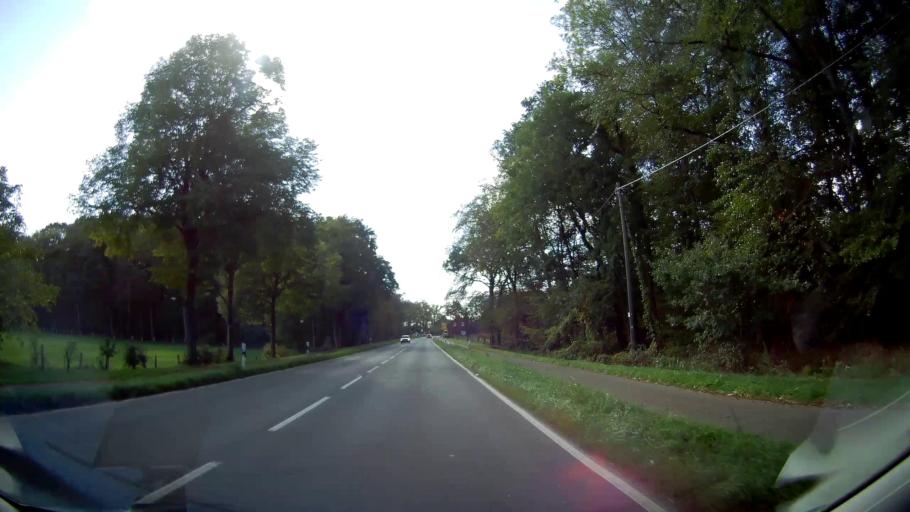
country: DE
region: North Rhine-Westphalia
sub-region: Regierungsbezirk Dusseldorf
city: Dinslaken
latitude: 51.5860
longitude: 6.7791
